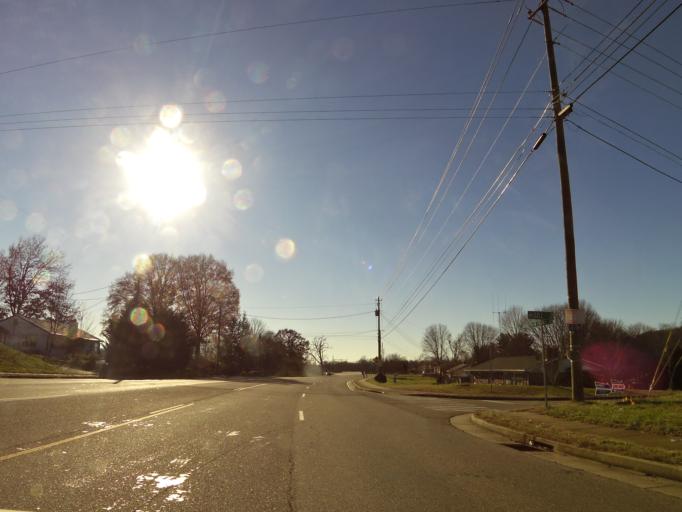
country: US
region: Tennessee
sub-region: Knox County
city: Knoxville
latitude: 36.0364
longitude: -84.0167
